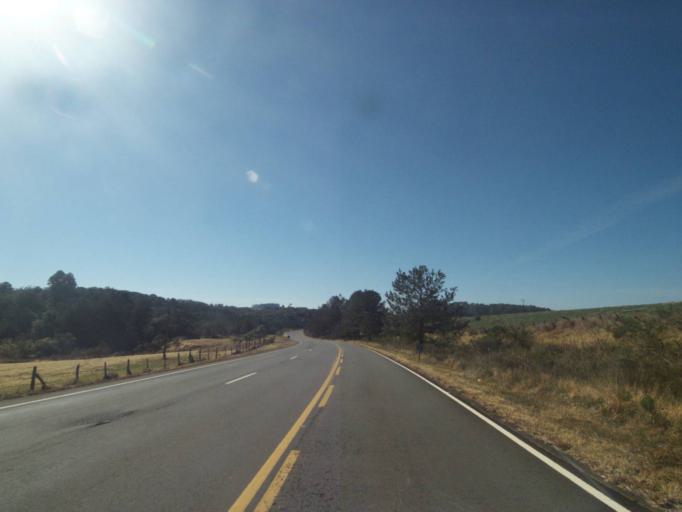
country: BR
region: Parana
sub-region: Tibagi
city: Tibagi
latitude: -24.4686
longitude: -50.5001
